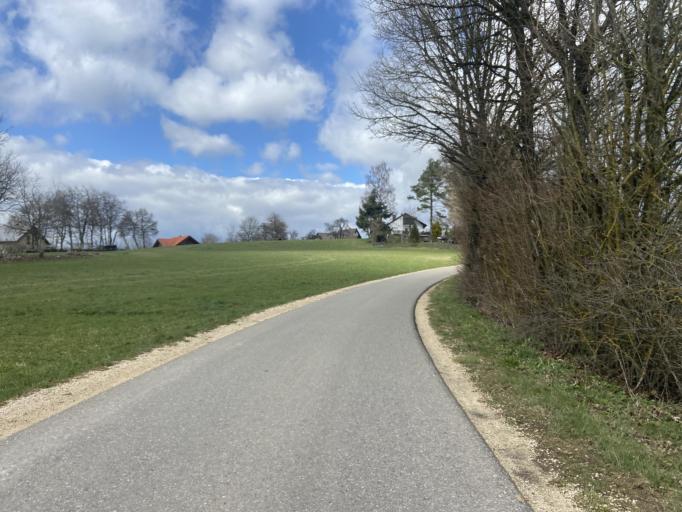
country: DE
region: Baden-Wuerttemberg
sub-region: Tuebingen Region
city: Bingen
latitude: 48.1466
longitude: 9.2406
